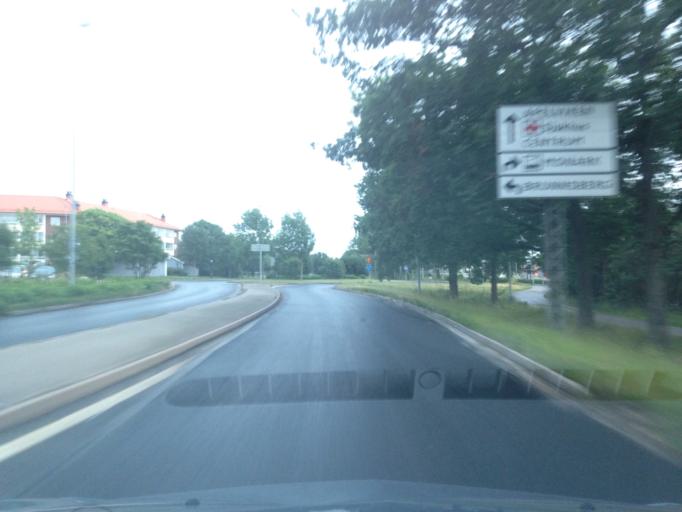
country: SE
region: Halland
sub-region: Varbergs Kommun
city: Varberg
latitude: 57.1173
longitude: 12.2610
